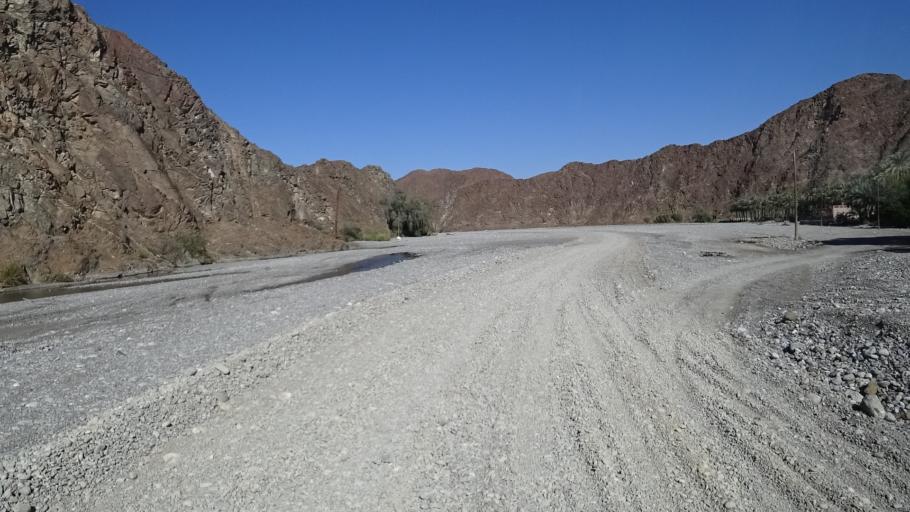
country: OM
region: Al Batinah
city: Bayt al `Awabi
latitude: 23.3901
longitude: 57.6605
